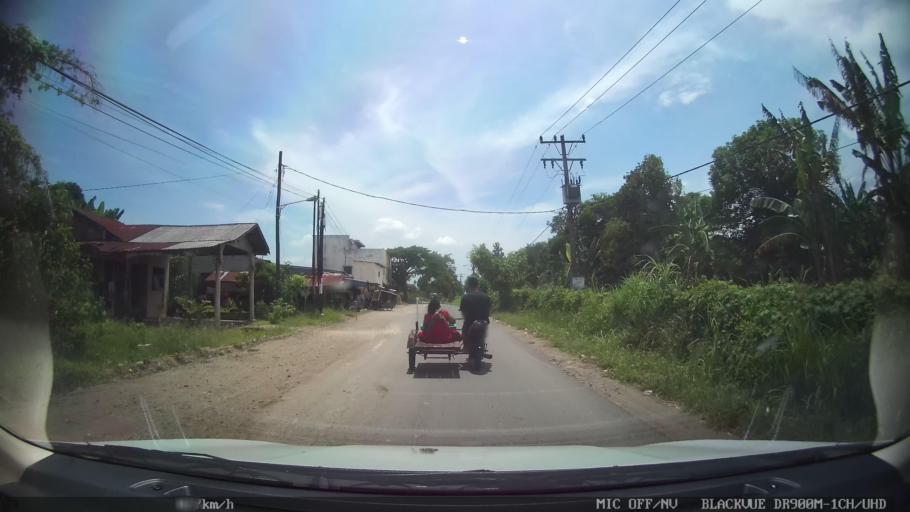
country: ID
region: North Sumatra
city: Binjai
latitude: 3.5940
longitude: 98.4946
